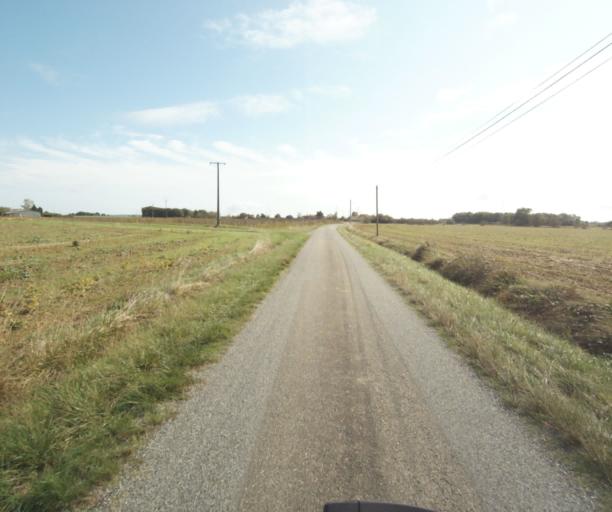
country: FR
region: Midi-Pyrenees
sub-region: Departement du Tarn-et-Garonne
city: Verdun-sur-Garonne
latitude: 43.8455
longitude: 1.1731
